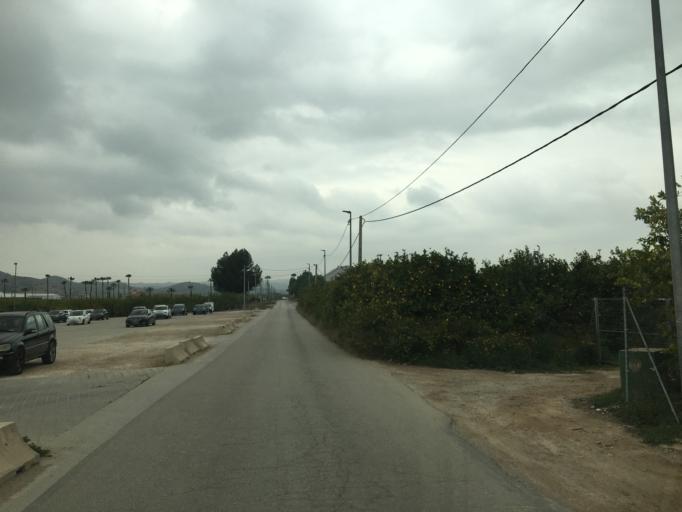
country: ES
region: Murcia
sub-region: Murcia
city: Santomera
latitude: 38.0809
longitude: -1.0526
